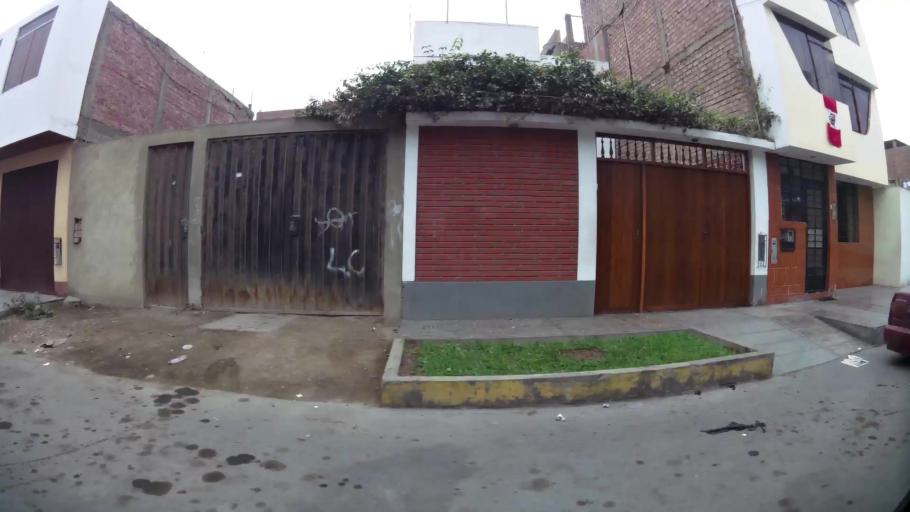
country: PE
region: Lima
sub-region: Lima
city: Independencia
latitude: -11.9414
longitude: -77.0849
